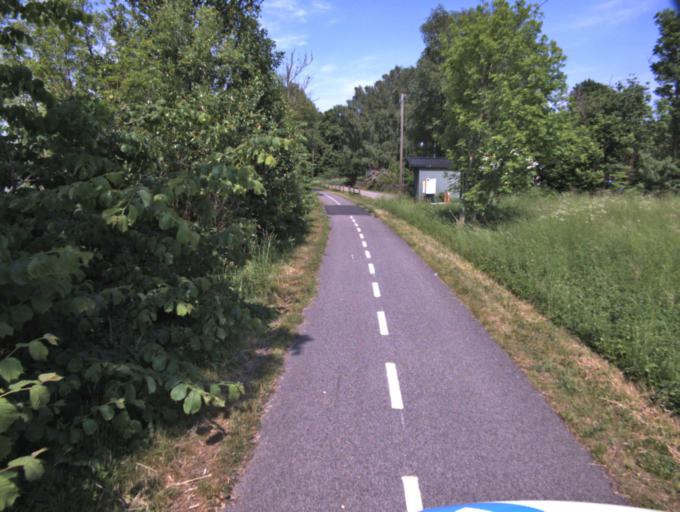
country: SE
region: Skane
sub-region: Kristianstads Kommun
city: Fjalkinge
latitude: 56.0873
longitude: 14.2325
